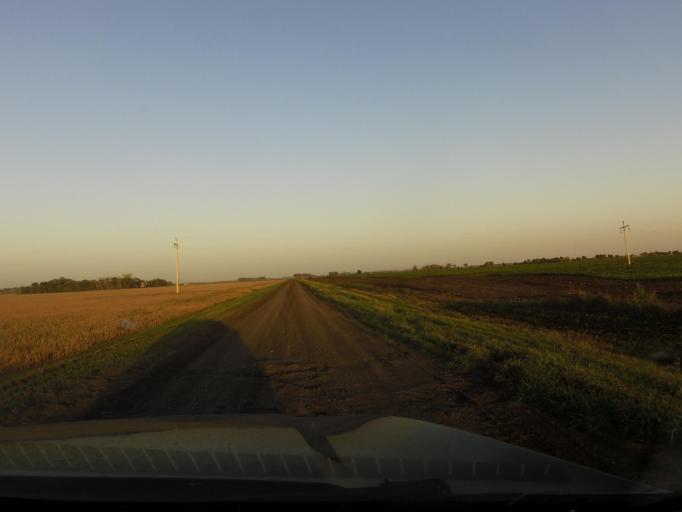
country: US
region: North Dakota
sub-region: Walsh County
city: Grafton
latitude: 48.3830
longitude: -97.2336
